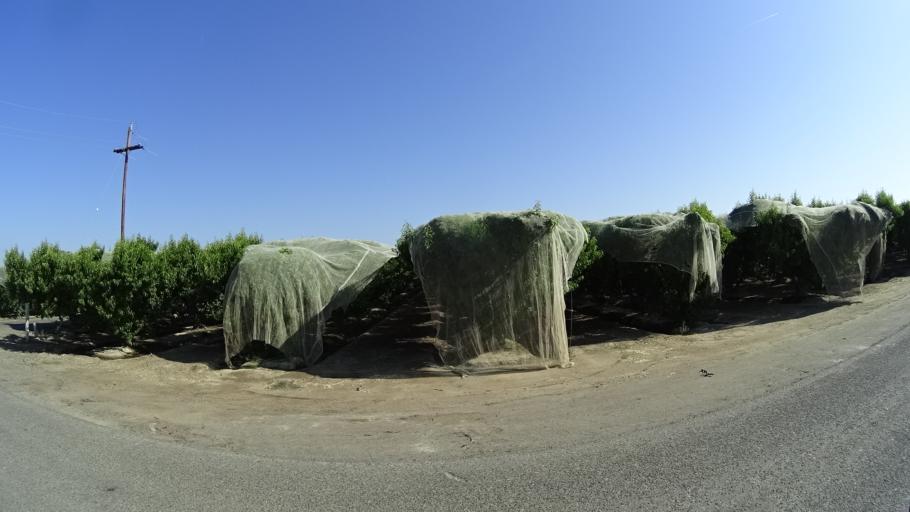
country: US
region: California
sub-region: Kings County
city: Lucerne
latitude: 36.3864
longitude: -119.6487
